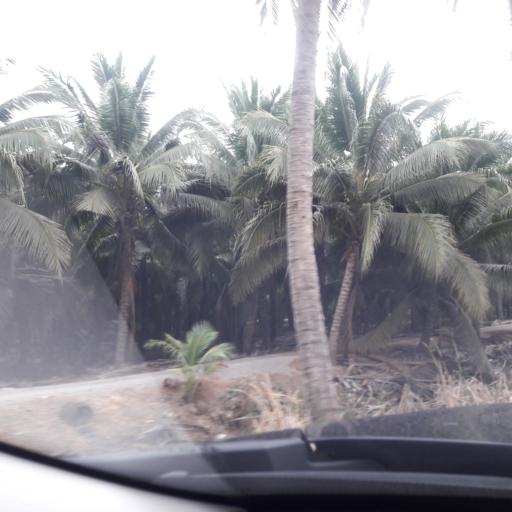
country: TH
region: Ratchaburi
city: Damnoen Saduak
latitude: 13.5658
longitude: 99.9448
